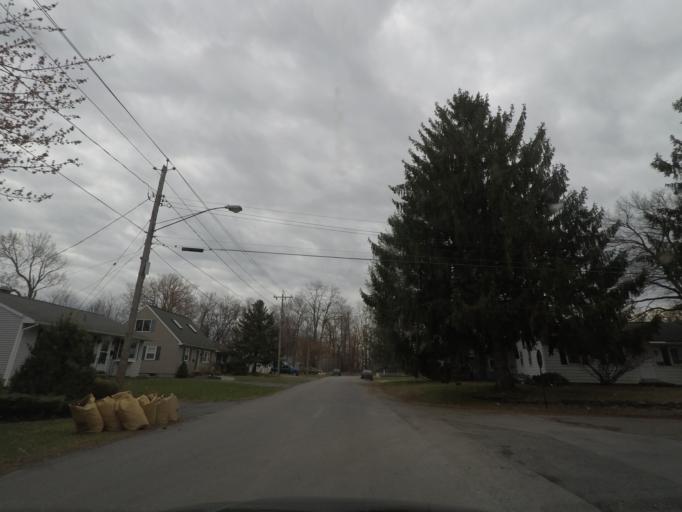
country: US
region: New York
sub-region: Rensselaer County
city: Hampton Manor
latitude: 42.6180
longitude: -73.7176
